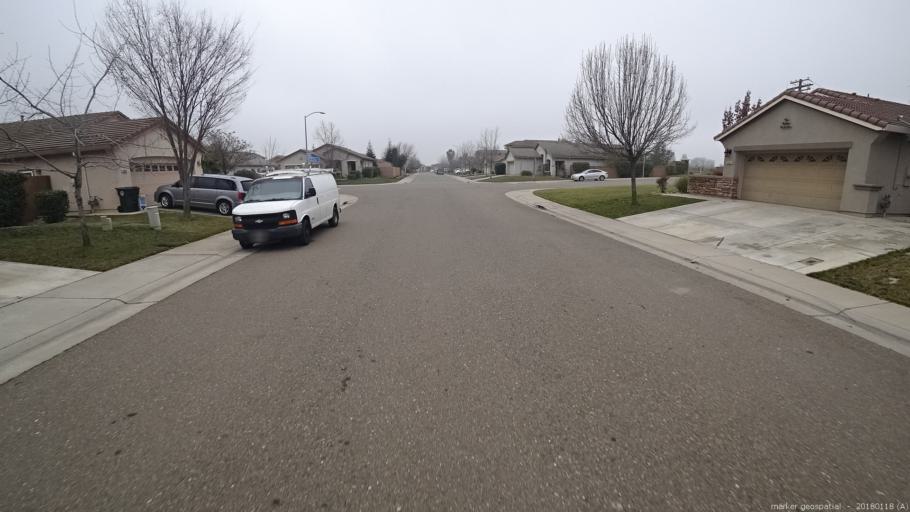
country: US
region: California
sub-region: Sacramento County
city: Rancho Cordova
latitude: 38.5742
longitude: -121.2882
